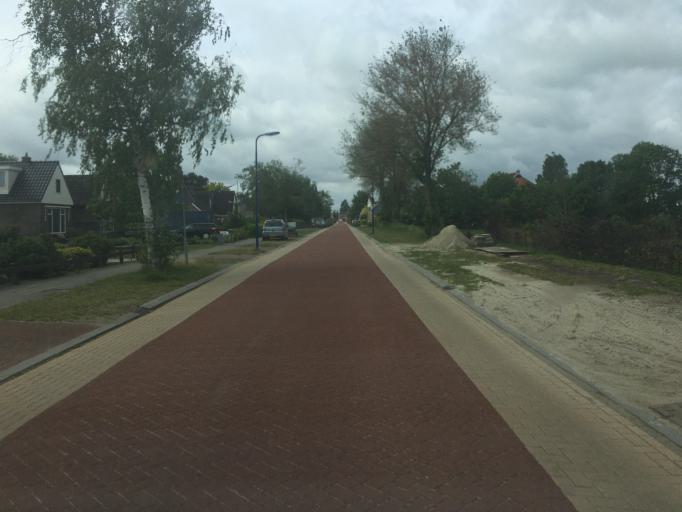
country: NL
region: Friesland
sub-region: Gemeente Lemsterland
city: Echtenerbrug
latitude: 52.8763
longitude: 5.8270
